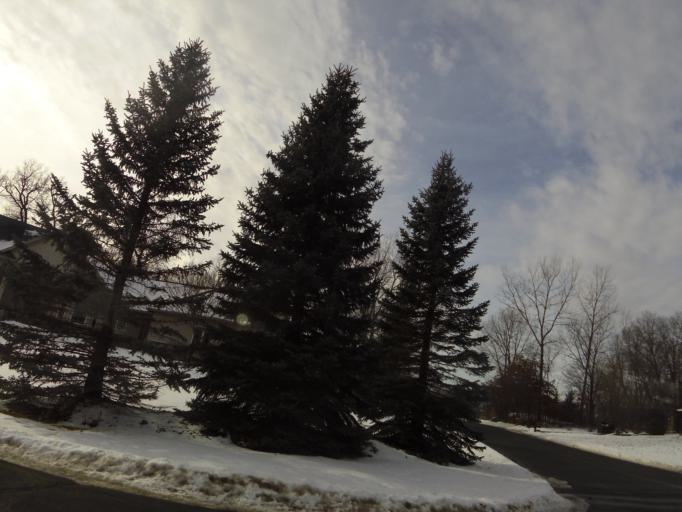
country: US
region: Minnesota
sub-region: Dakota County
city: Lakeville
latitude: 44.6843
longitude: -93.2699
